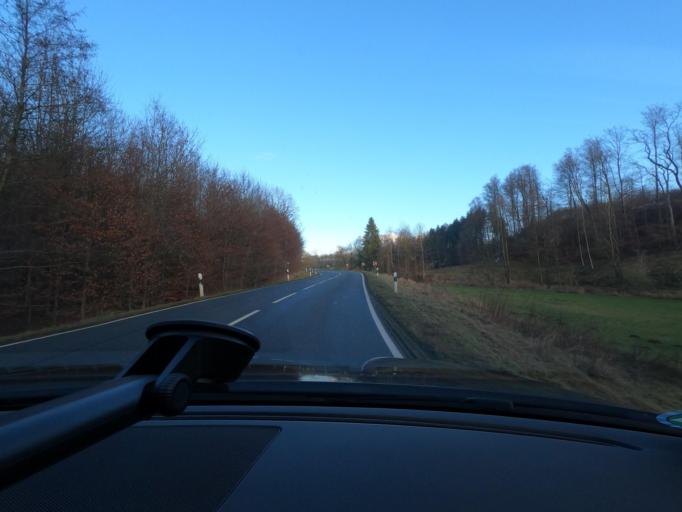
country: DE
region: Lower Saxony
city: Rhumspringe
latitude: 51.6012
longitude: 10.3204
